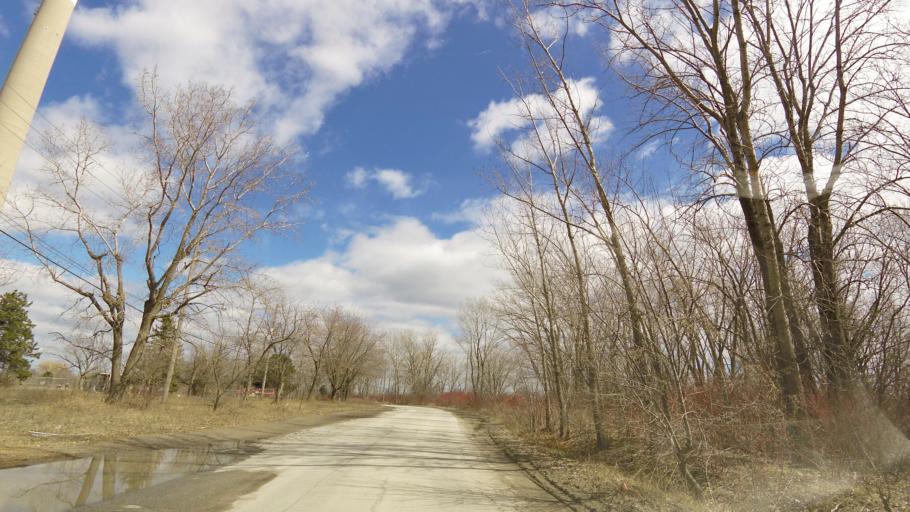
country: CA
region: Ontario
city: Toronto
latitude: 43.6448
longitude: -79.3358
